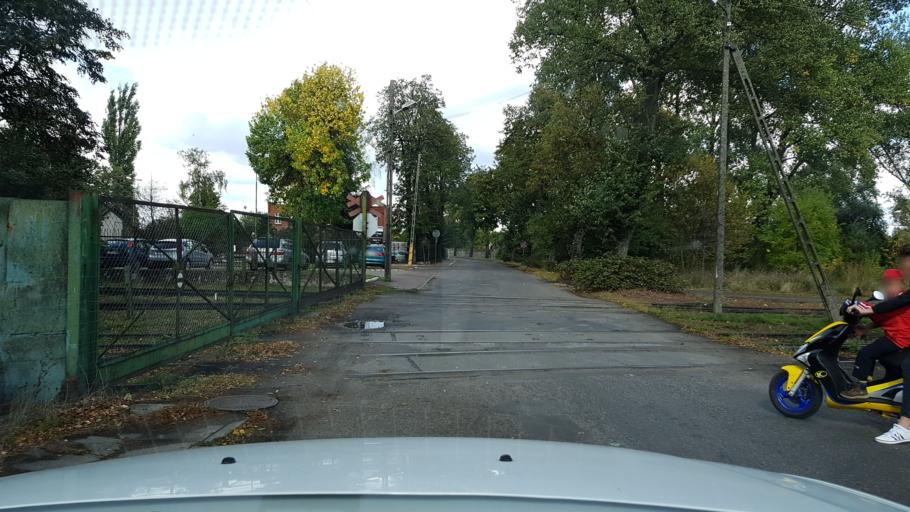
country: PL
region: West Pomeranian Voivodeship
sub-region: Powiat gryfinski
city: Gryfino
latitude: 53.2821
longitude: 14.4991
